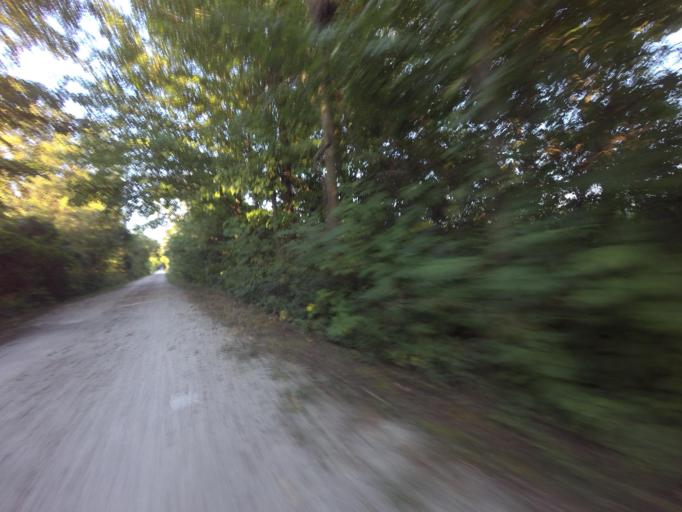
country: CA
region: Ontario
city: Brampton
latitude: 43.8789
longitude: -79.8522
